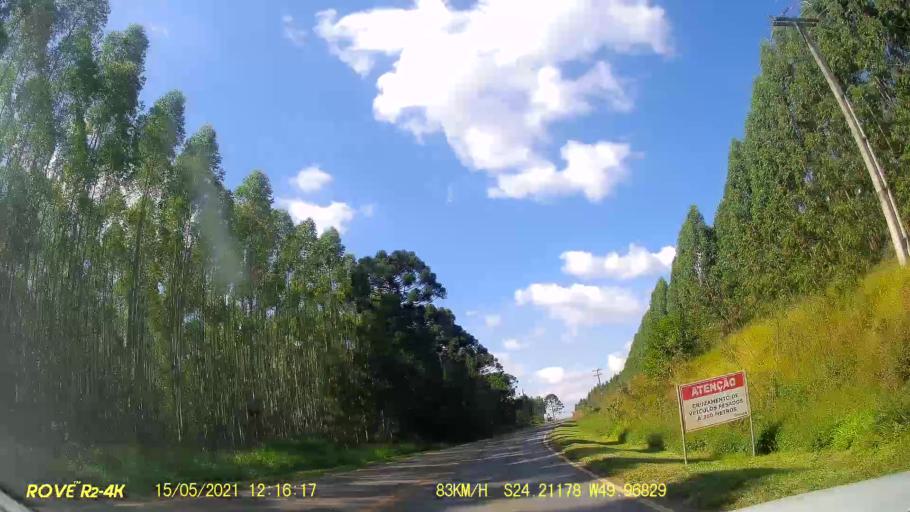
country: BR
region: Parana
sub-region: Jaguariaiva
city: Jaguariaiva
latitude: -24.2117
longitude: -49.9682
